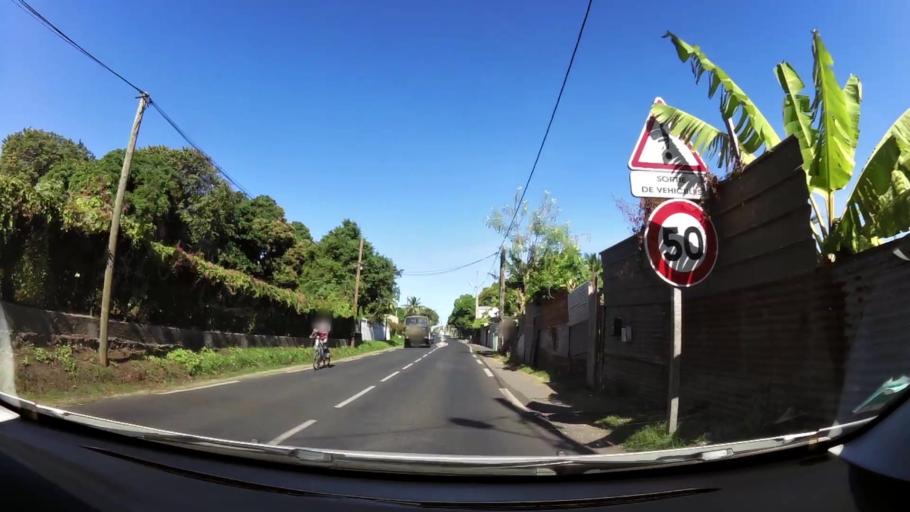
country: YT
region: Pamandzi
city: Pamandzi
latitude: -12.7936
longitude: 45.2719
